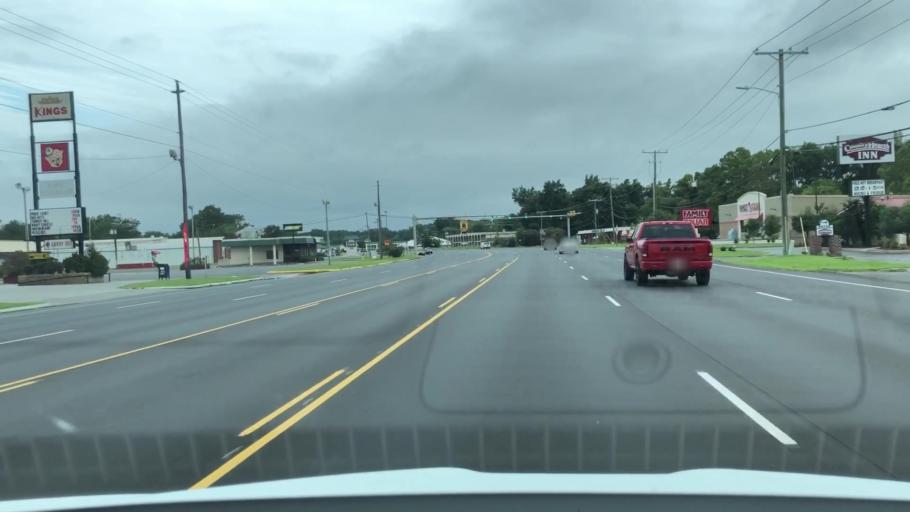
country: US
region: North Carolina
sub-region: Lenoir County
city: Kinston
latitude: 35.2412
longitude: -77.5778
